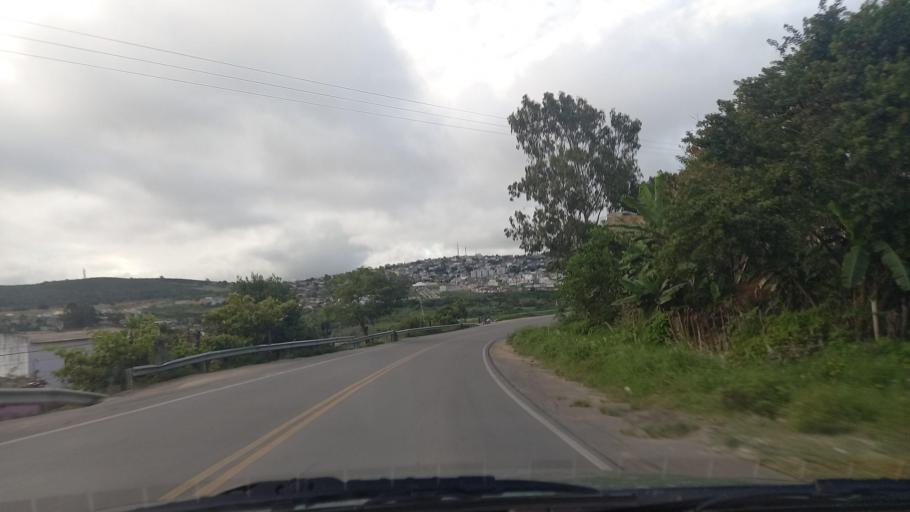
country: BR
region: Pernambuco
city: Garanhuns
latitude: -8.8990
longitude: -36.5030
